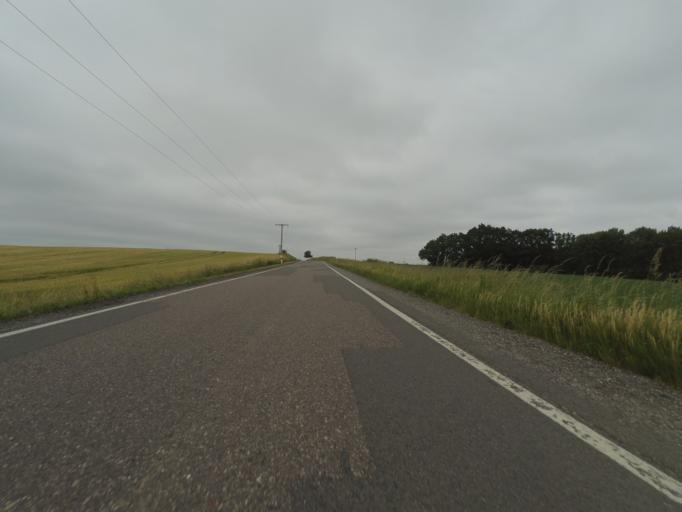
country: DE
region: Mecklenburg-Vorpommern
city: Gaegelow
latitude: 53.6958
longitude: 11.8897
